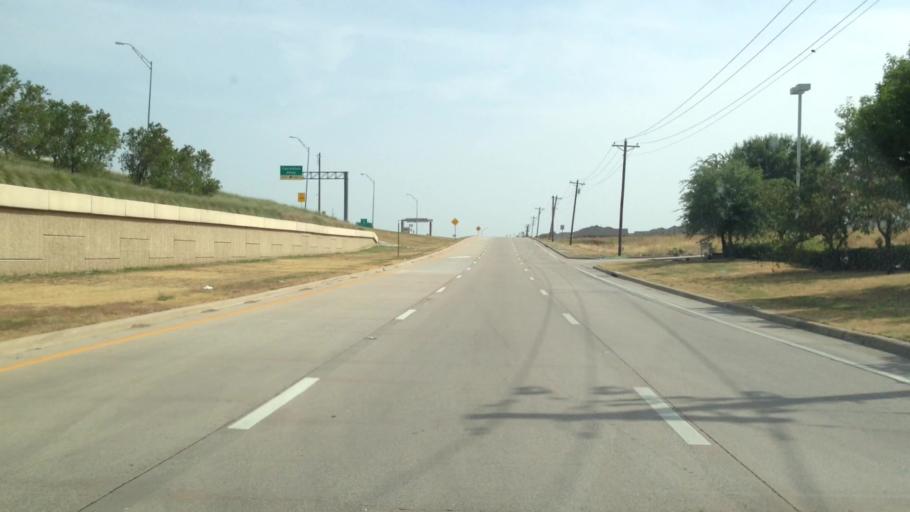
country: US
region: Texas
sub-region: Denton County
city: Lewisville
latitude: 33.0223
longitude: -96.9336
